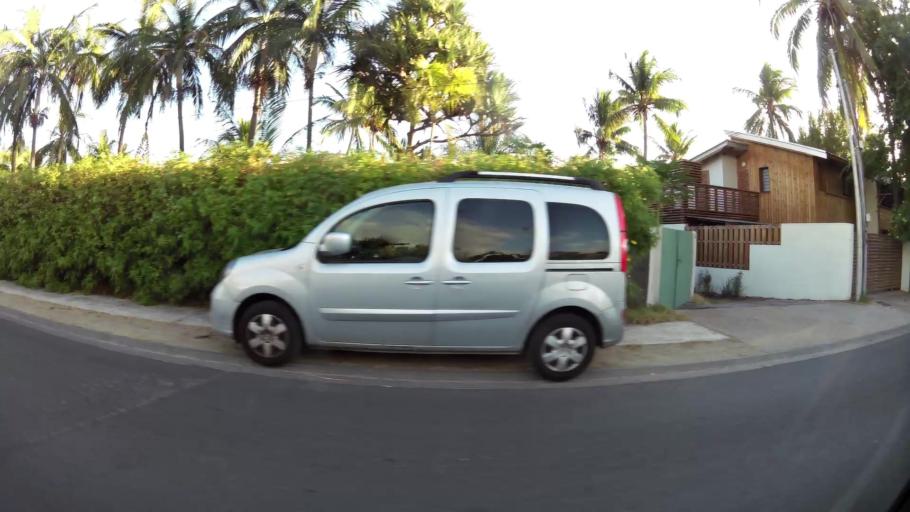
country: RE
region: Reunion
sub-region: Reunion
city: Trois-Bassins
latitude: -21.0997
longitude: 55.2433
